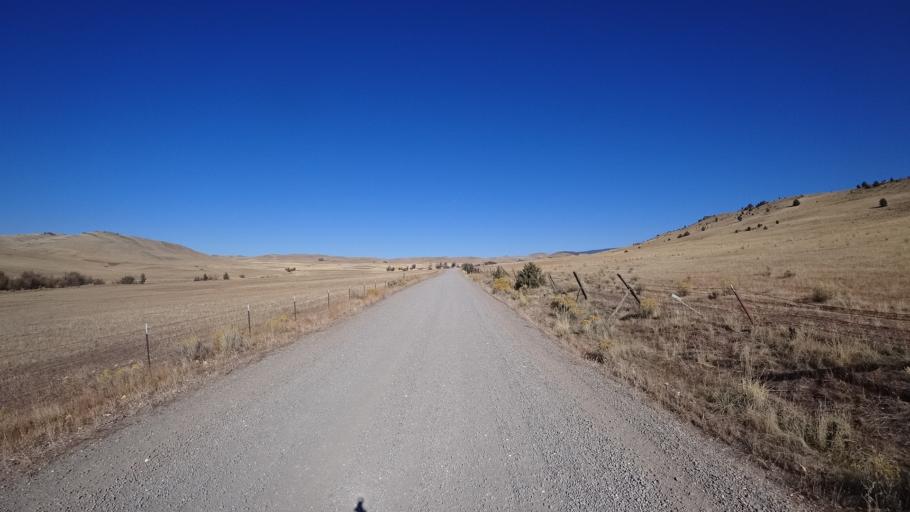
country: US
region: California
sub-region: Siskiyou County
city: Montague
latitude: 41.7348
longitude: -122.3690
